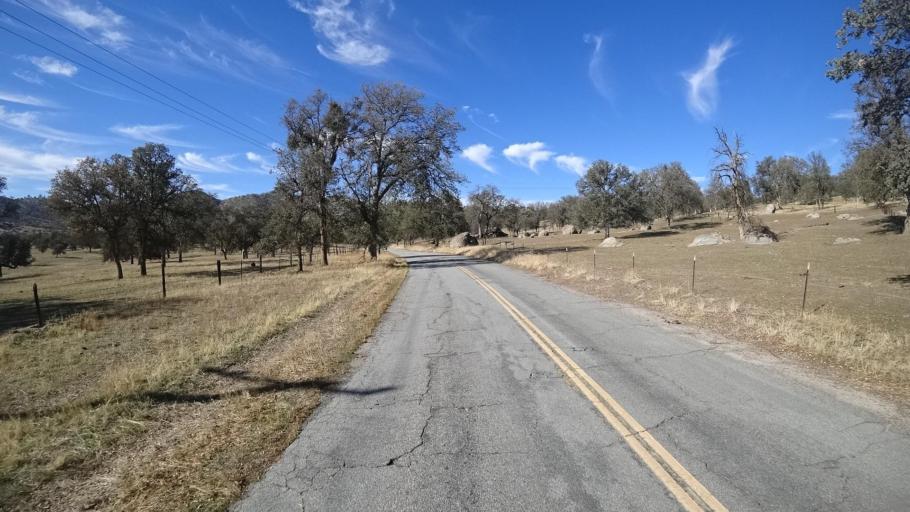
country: US
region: California
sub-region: Kern County
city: Alta Sierra
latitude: 35.6221
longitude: -118.7411
